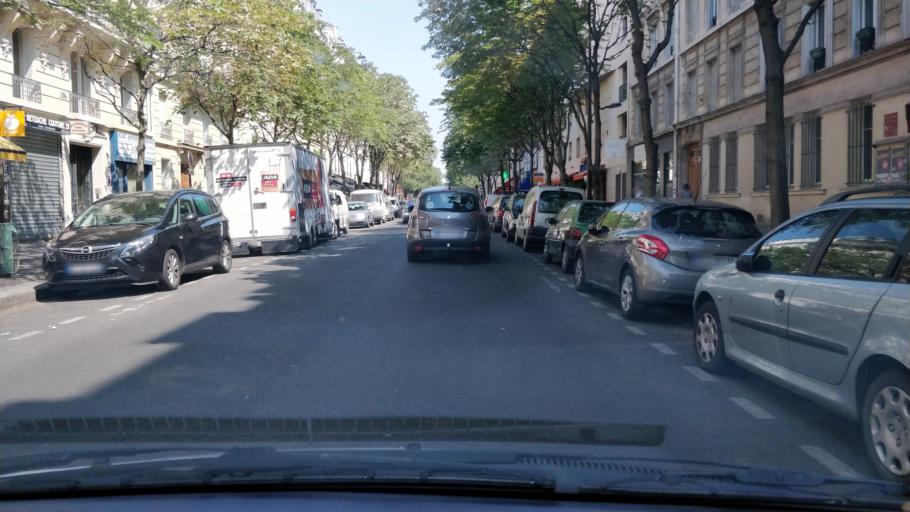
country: FR
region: Ile-de-France
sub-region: Departement du Val-de-Marne
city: Ivry-sur-Seine
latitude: 48.8457
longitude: 2.3836
